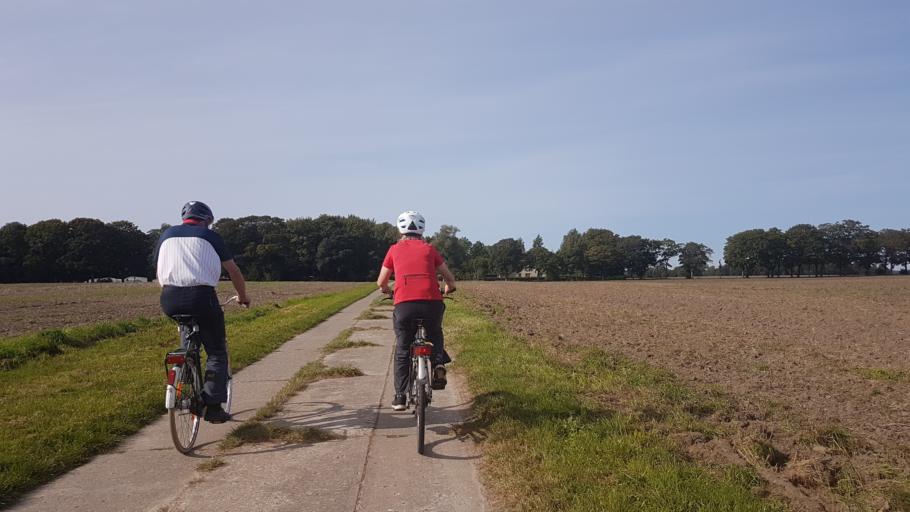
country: DE
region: Mecklenburg-Vorpommern
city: Gingst
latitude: 54.4401
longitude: 13.1882
